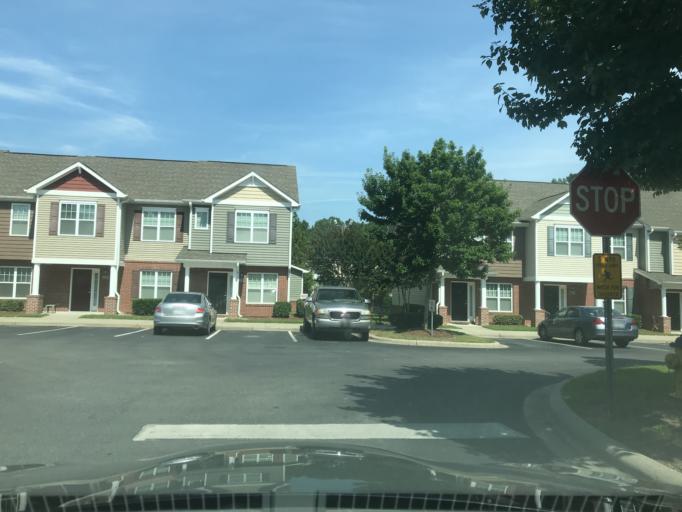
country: US
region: North Carolina
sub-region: Wake County
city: Wendell
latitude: 35.7826
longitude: -78.3610
